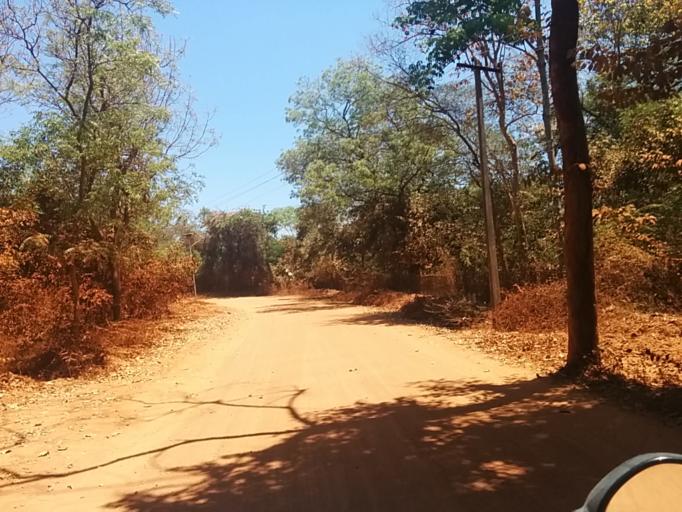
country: IN
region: Tamil Nadu
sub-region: Villupuram
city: Auroville
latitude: 12.0057
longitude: 79.8077
